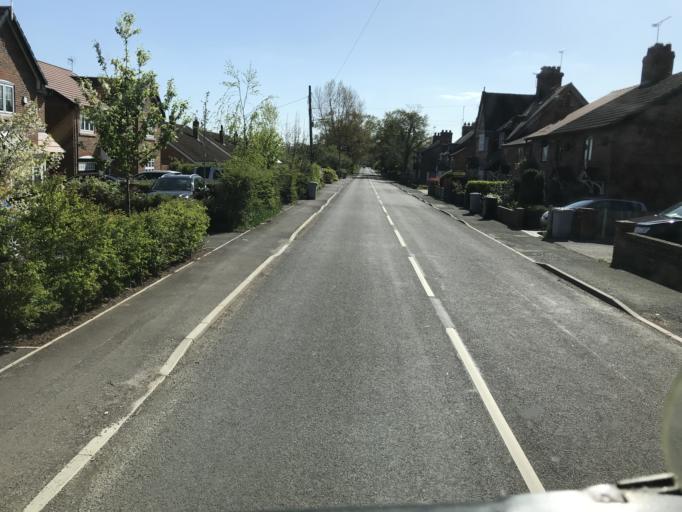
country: GB
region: England
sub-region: Cheshire East
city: Nantwich
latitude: 53.1051
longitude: -2.5119
